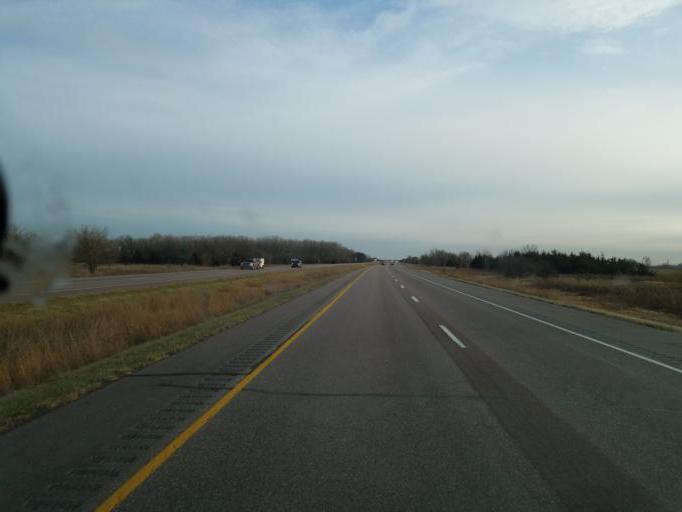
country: US
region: Nebraska
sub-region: Thurston County
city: Macy
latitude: 42.1395
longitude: -96.2116
